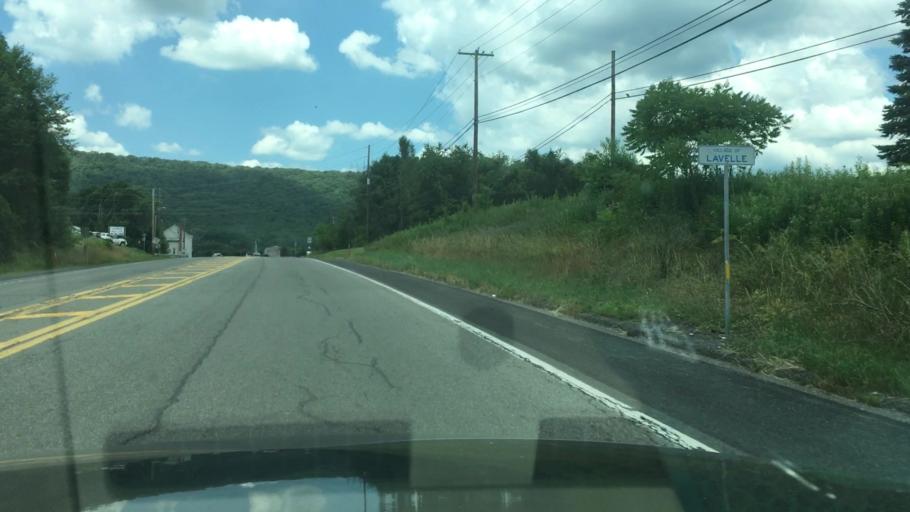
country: US
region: Pennsylvania
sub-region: Schuylkill County
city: Ashland
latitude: 40.7568
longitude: -76.3824
